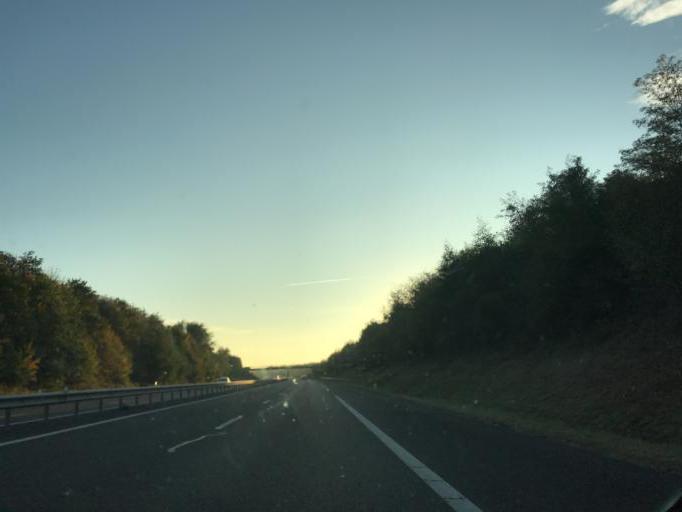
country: FR
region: Bourgogne
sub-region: Departement de l'Yonne
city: Paron
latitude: 48.2016
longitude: 3.2062
